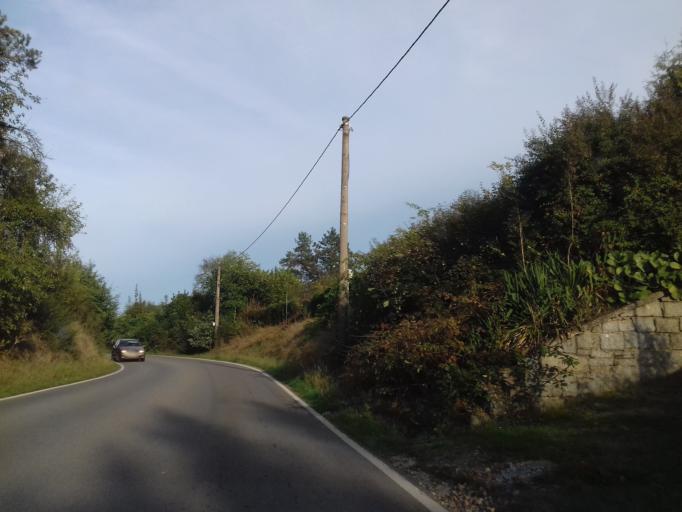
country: CZ
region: Central Bohemia
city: Kamenny Privoz
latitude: 49.8659
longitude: 14.5021
